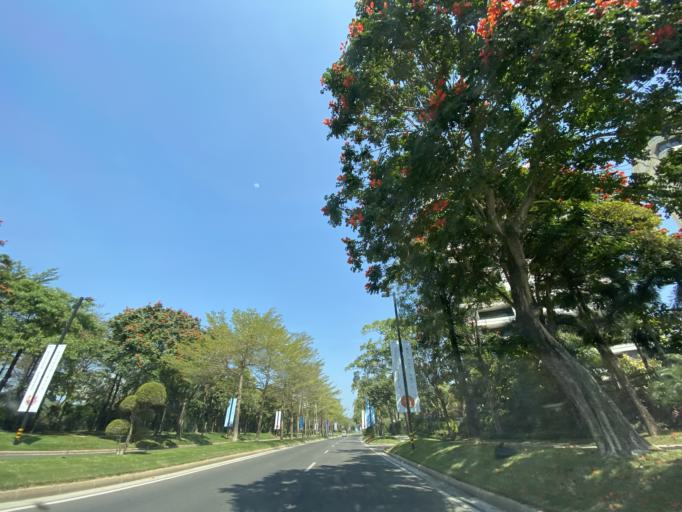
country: CN
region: Hainan
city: Yingzhou
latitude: 18.4195
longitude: 109.8443
